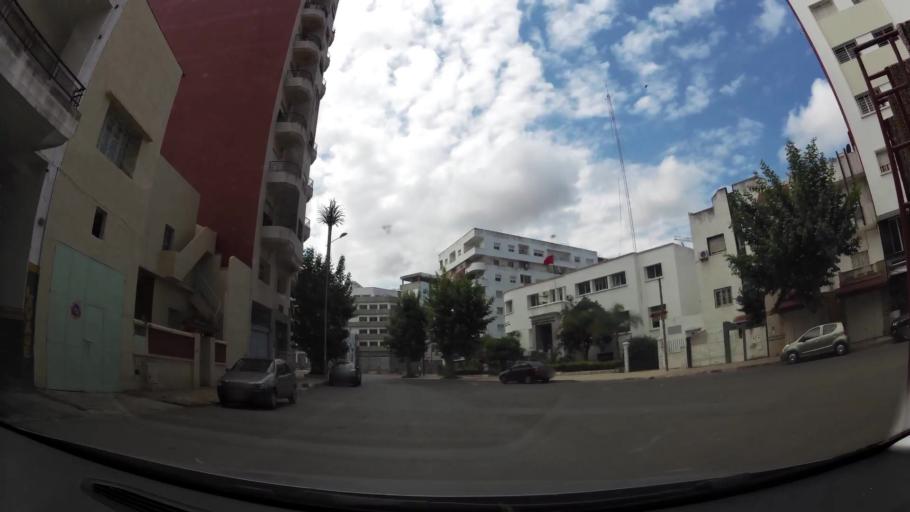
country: MA
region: Gharb-Chrarda-Beni Hssen
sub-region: Kenitra Province
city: Kenitra
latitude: 34.2564
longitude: -6.5871
